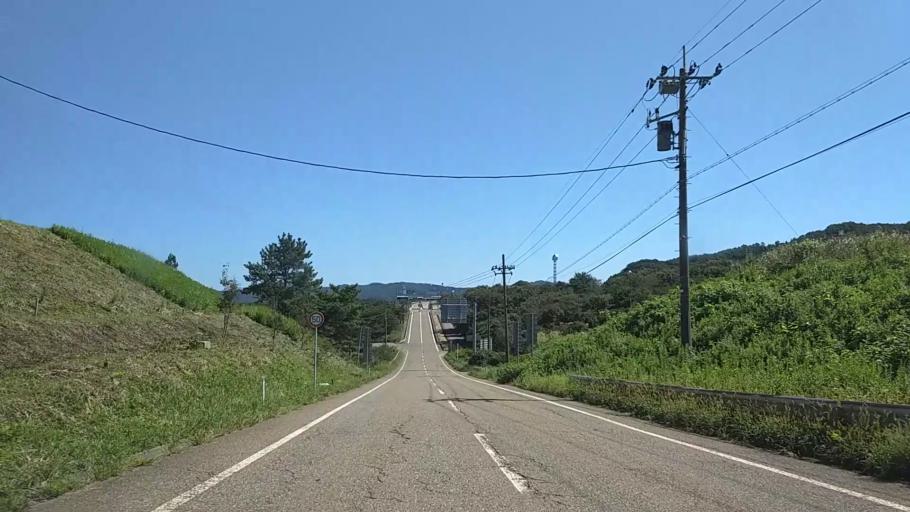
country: JP
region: Niigata
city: Joetsu
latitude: 37.1700
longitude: 138.1073
